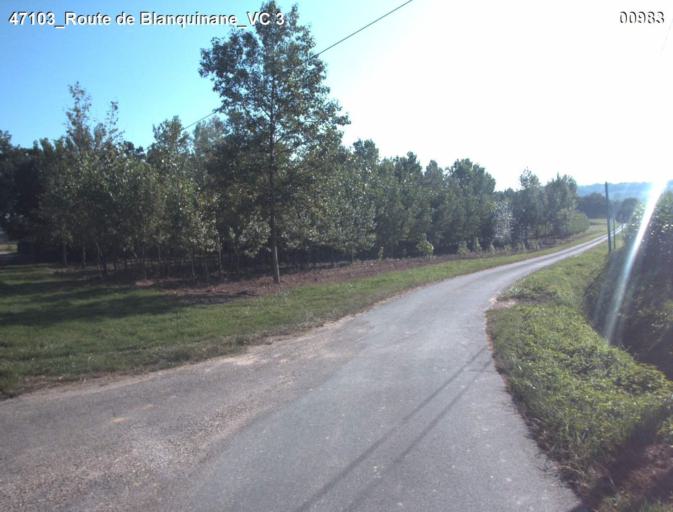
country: FR
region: Aquitaine
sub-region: Departement du Lot-et-Garonne
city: Nerac
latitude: 44.0834
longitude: 0.3521
